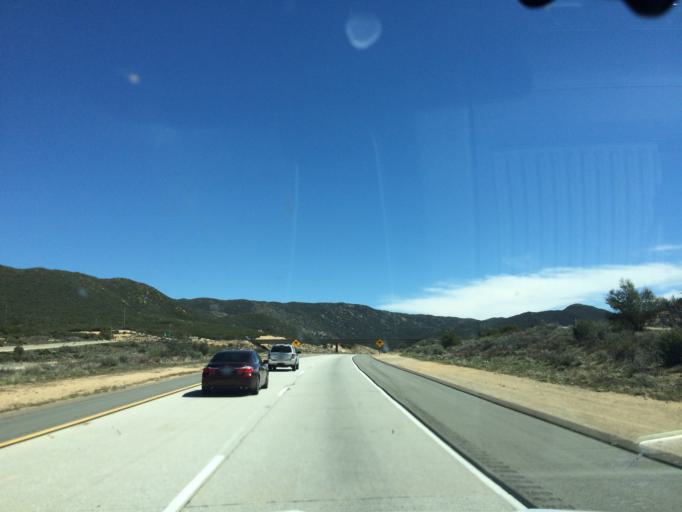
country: US
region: California
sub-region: San Diego County
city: Pine Valley
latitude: 32.8120
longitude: -116.5142
